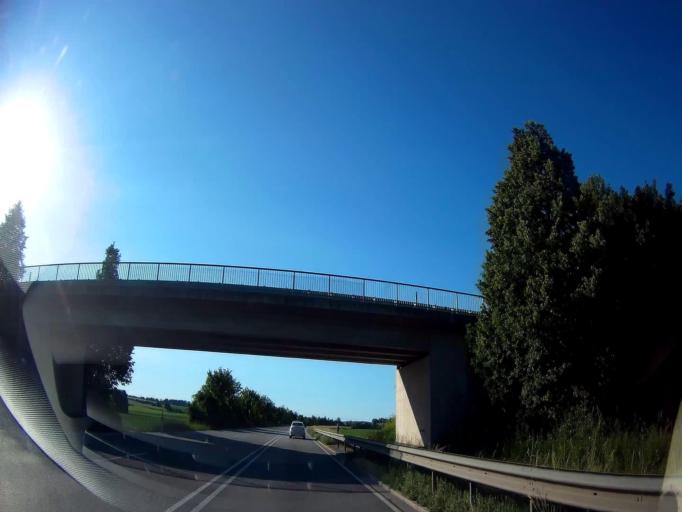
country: DE
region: Bavaria
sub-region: Lower Bavaria
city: Pilsting
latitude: 48.7273
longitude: 12.6622
